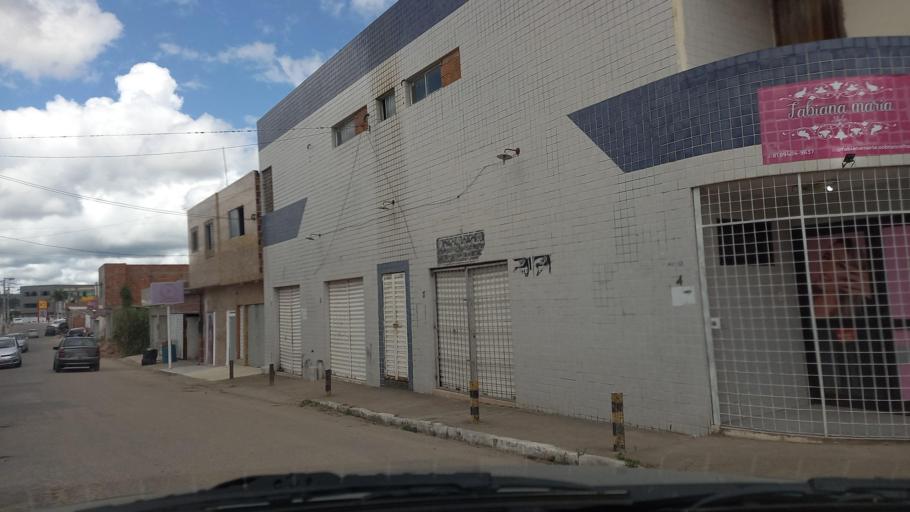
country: BR
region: Pernambuco
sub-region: Caruaru
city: Caruaru
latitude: -8.2763
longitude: -35.9413
